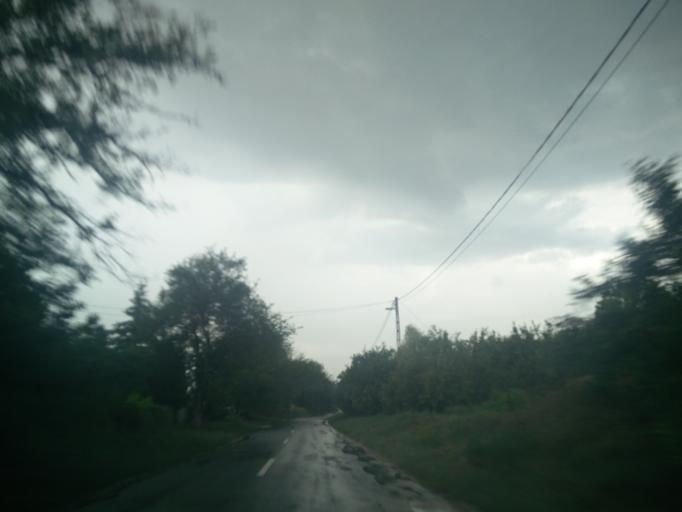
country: HU
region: Fejer
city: Lovasbereny
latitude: 47.2961
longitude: 18.5684
